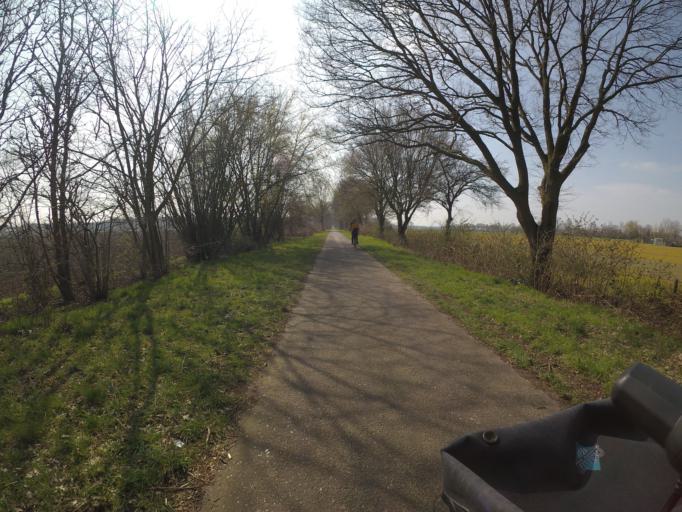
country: NL
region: North Brabant
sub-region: Gemeente Goirle
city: Goirle
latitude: 51.5158
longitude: 5.0056
